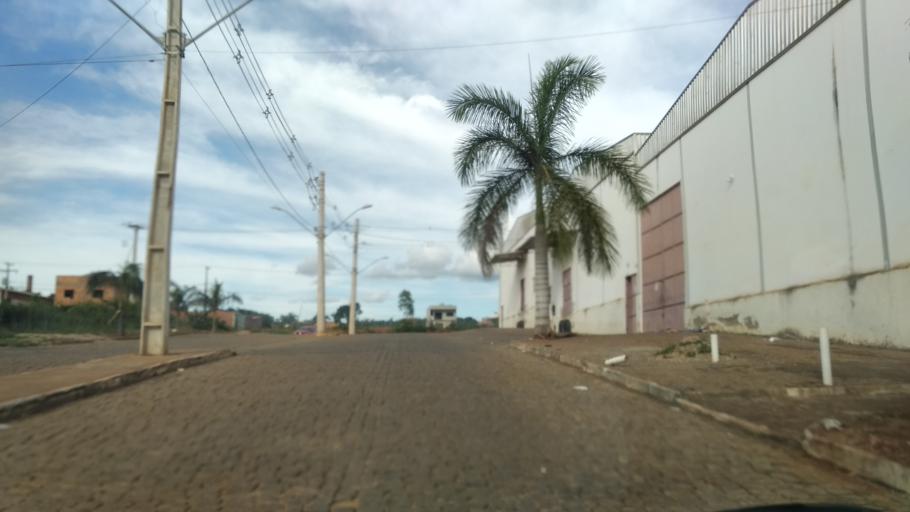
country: BR
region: Bahia
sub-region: Caetite
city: Caetite
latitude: -14.0581
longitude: -42.4938
